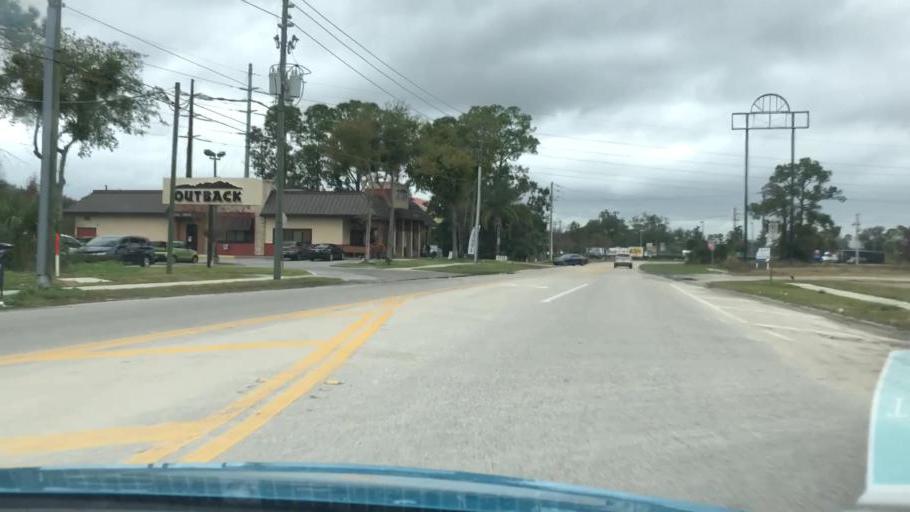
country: US
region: Florida
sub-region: Seminole County
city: Lake Mary
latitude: 28.8127
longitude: -81.3342
